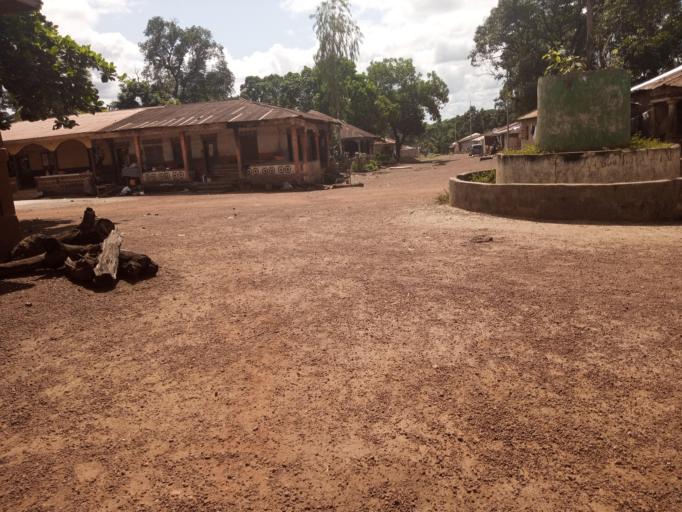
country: SL
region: Northern Province
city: Kamakwie
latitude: 9.4963
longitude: -12.2431
